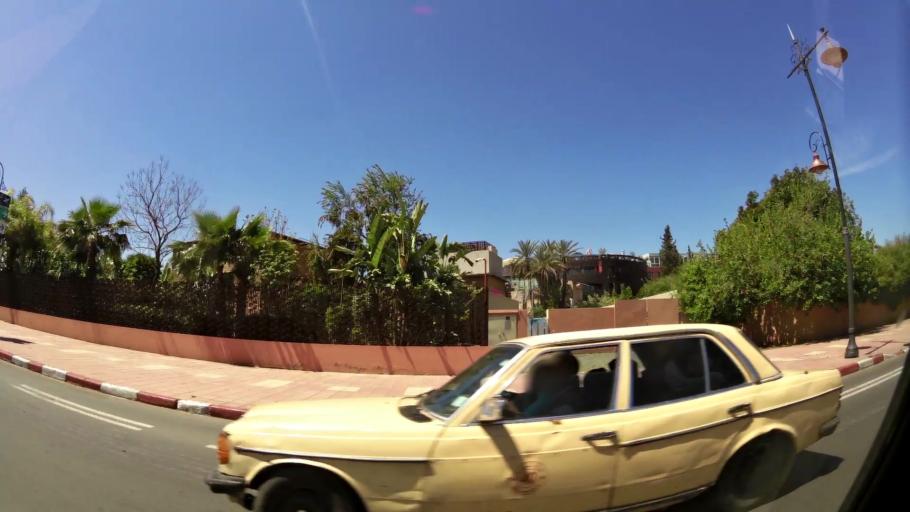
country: MA
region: Marrakech-Tensift-Al Haouz
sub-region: Marrakech
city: Marrakesh
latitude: 31.6225
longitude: -7.9995
